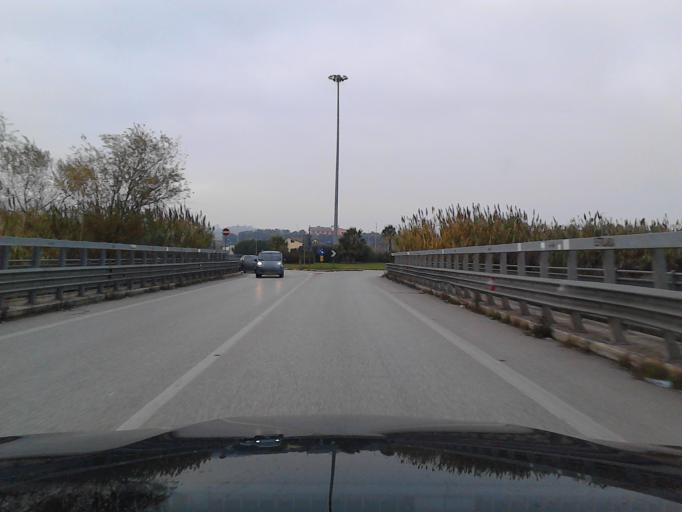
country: IT
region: Abruzzo
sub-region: Provincia di Teramo
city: Alba Adriatica
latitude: 42.8348
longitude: 13.9146
